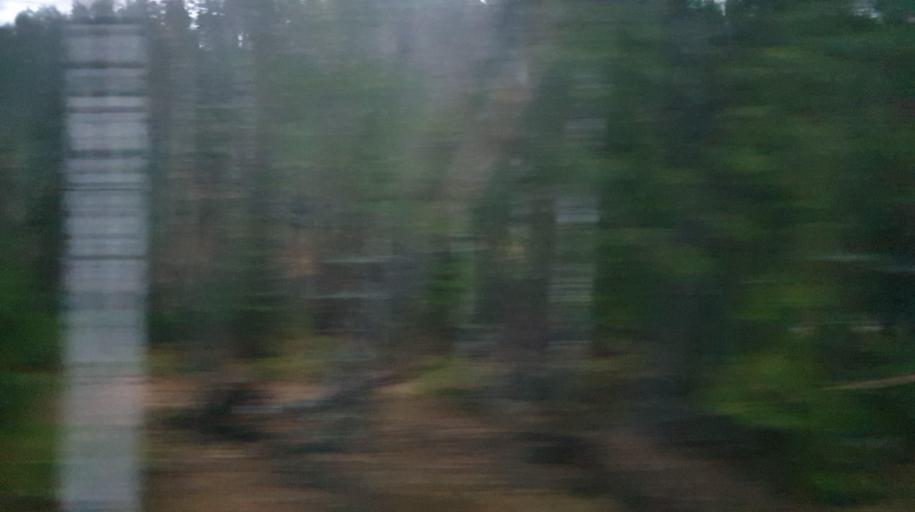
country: NO
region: Buskerud
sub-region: Sigdal
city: Prestfoss
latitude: 60.1031
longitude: 9.8115
